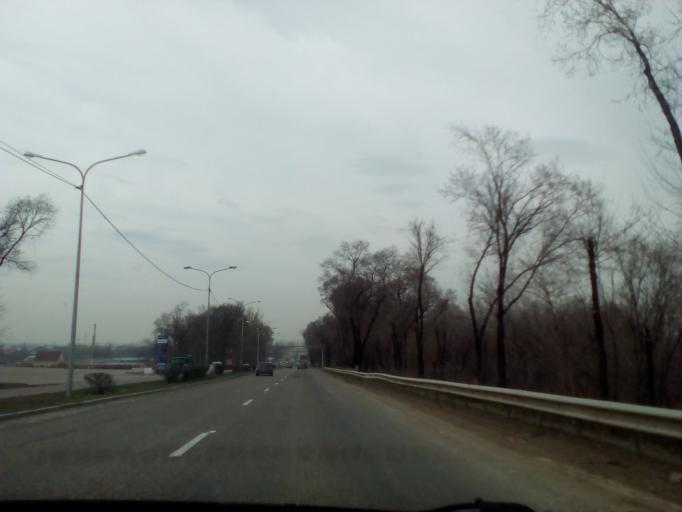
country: KZ
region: Almaty Oblysy
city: Burunday
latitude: 43.2165
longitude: 76.6615
